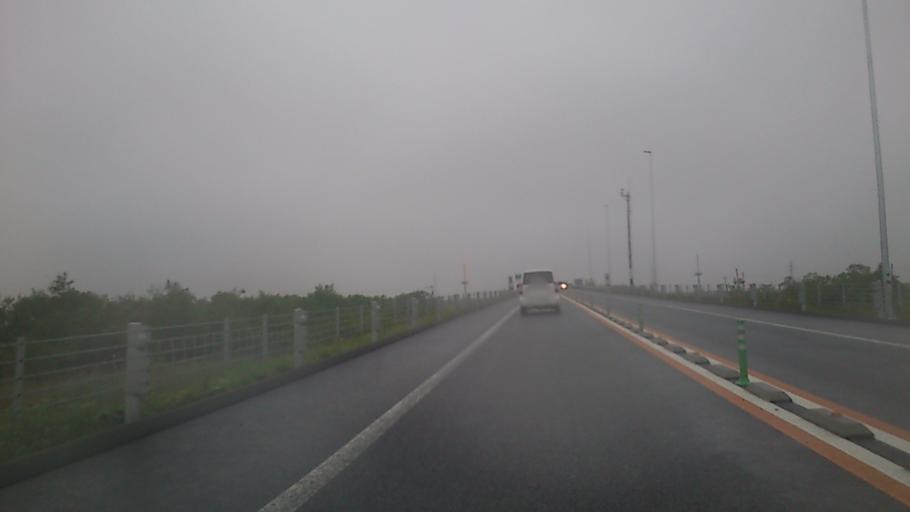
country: JP
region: Hokkaido
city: Kushiro
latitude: 43.0330
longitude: 144.3902
